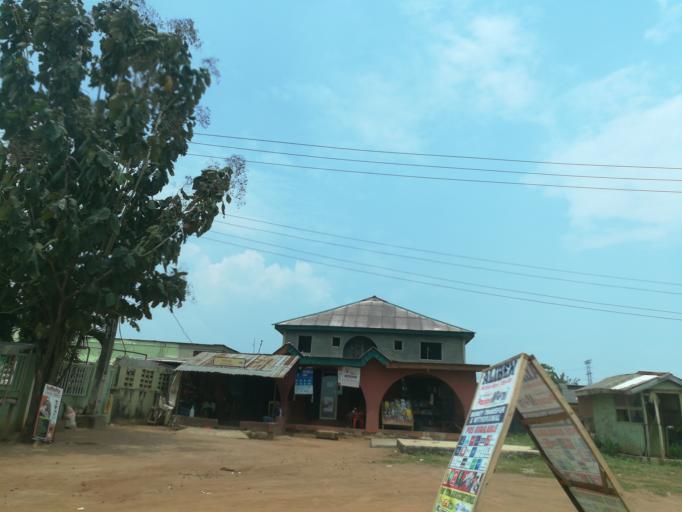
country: NG
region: Lagos
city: Ikorodu
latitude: 6.6042
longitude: 3.5867
